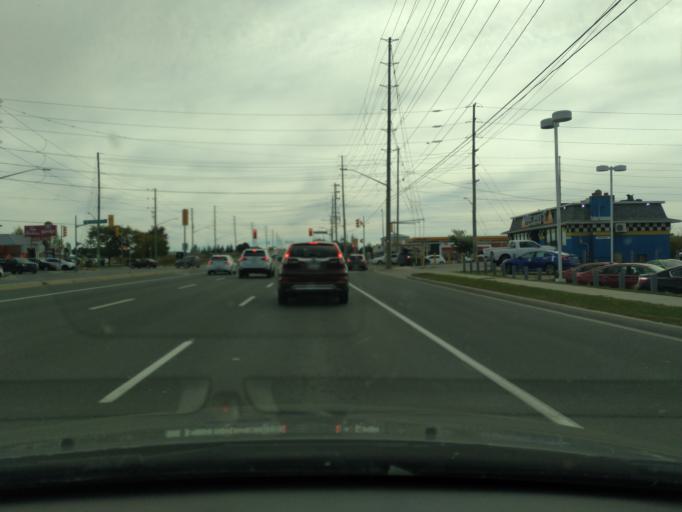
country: CA
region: Ontario
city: Oshawa
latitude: 43.8731
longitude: -78.9071
